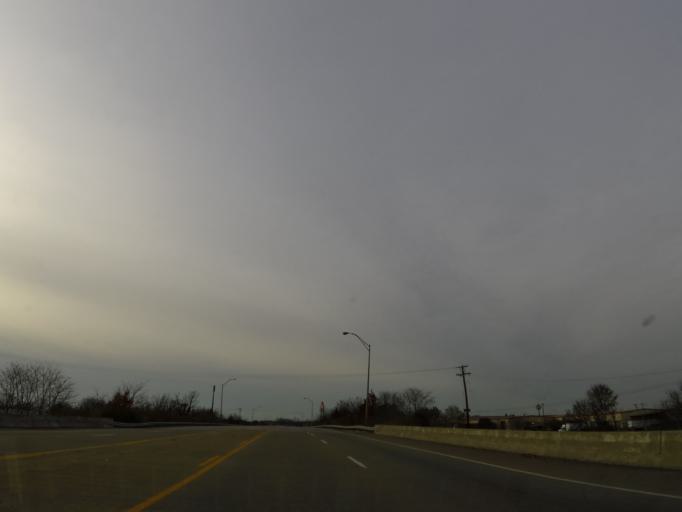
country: US
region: Kentucky
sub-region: Scott County
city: Georgetown
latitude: 38.2732
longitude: -84.5484
